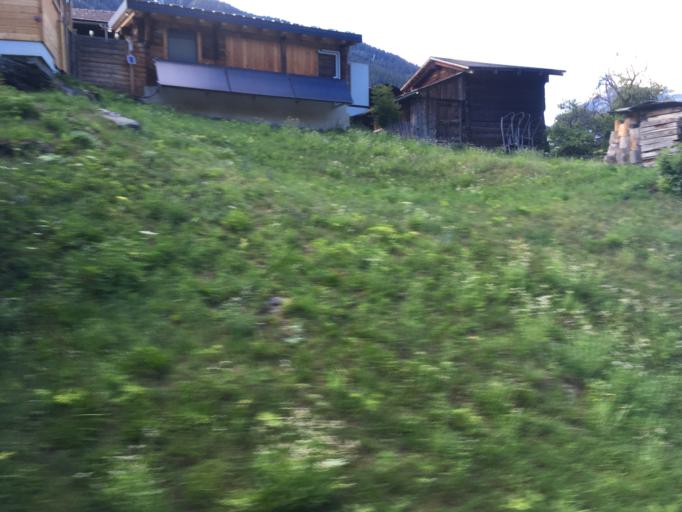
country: CH
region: Valais
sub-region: Goms District
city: Fiesch
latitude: 46.3877
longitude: 8.1203
